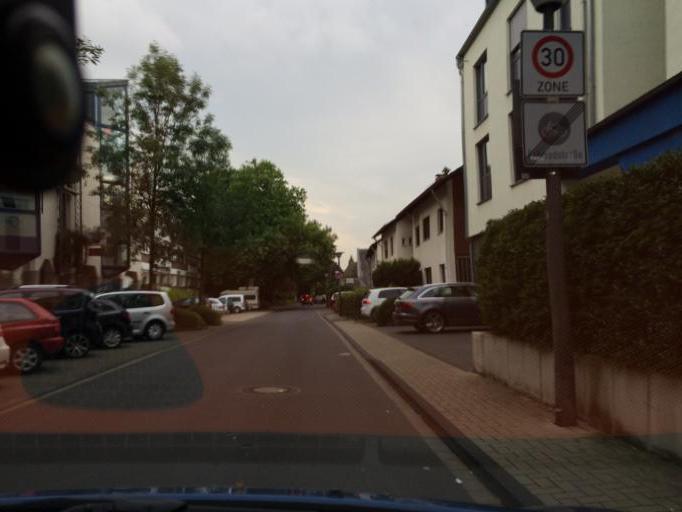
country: DE
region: North Rhine-Westphalia
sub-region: Regierungsbezirk Koln
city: Bonn
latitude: 50.7391
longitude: 7.1222
